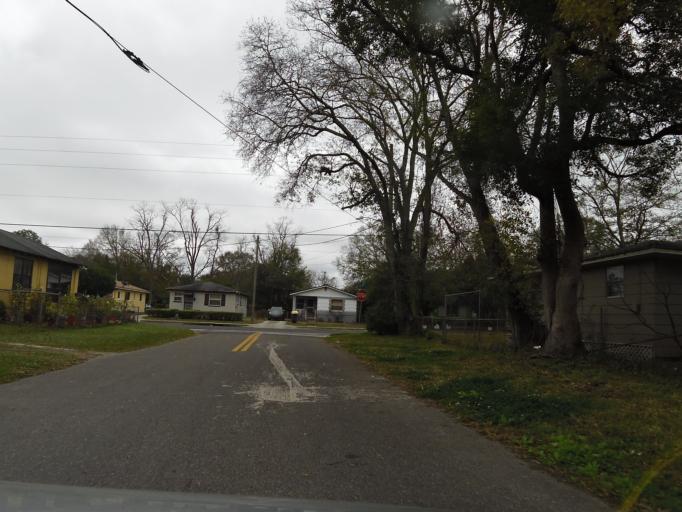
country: US
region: Florida
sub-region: Duval County
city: Jacksonville
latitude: 30.3517
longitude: -81.6845
